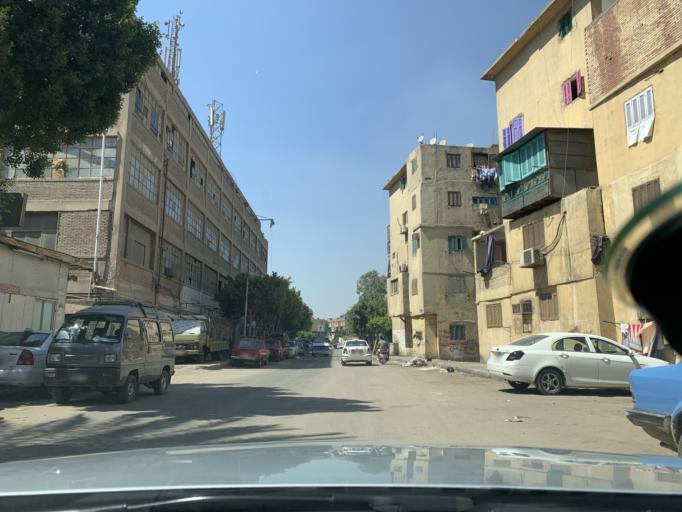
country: EG
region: Muhafazat al Qahirah
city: Cairo
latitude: 30.0734
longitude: 31.2570
